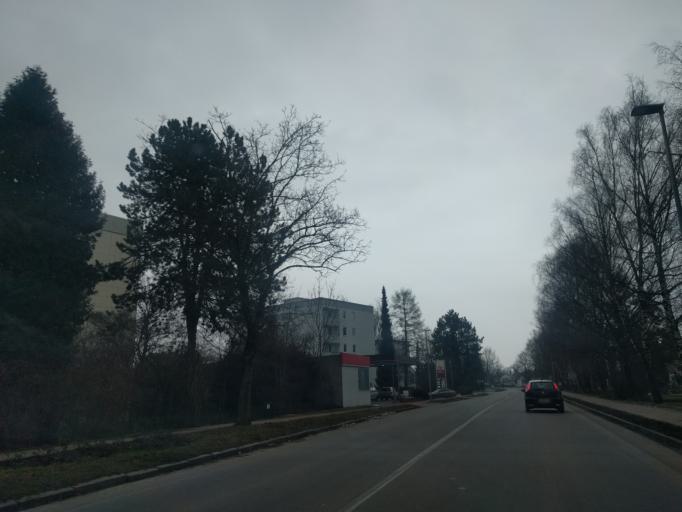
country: DE
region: Bavaria
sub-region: Swabia
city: Rain
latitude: 48.6944
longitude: 10.9087
